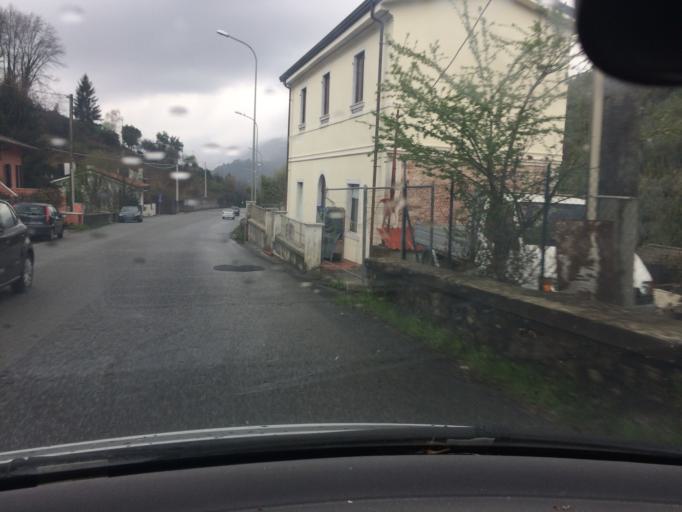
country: IT
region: Tuscany
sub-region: Provincia di Massa-Carrara
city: Massa
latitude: 44.0677
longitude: 10.1101
